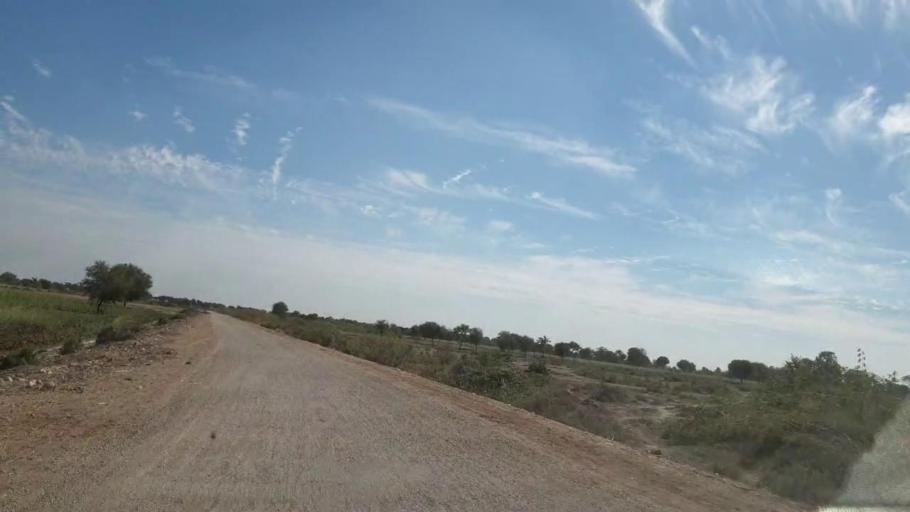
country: PK
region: Sindh
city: Pithoro
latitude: 25.5546
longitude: 69.2978
